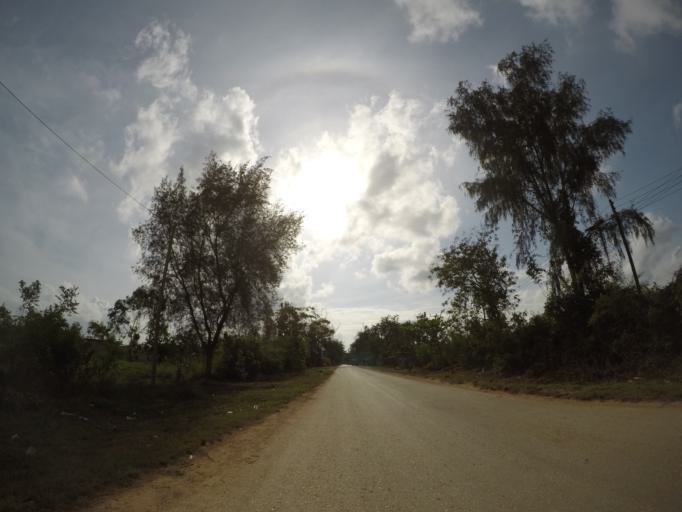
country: TZ
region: Zanzibar Central/South
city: Koani
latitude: -6.2256
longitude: 39.3189
